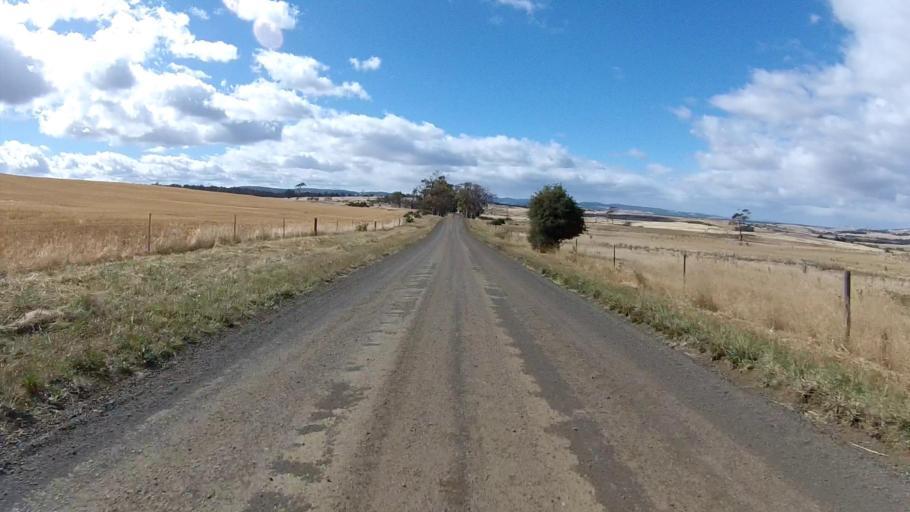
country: AU
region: Tasmania
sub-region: Northern Midlands
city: Evandale
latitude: -41.7170
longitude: 147.4205
